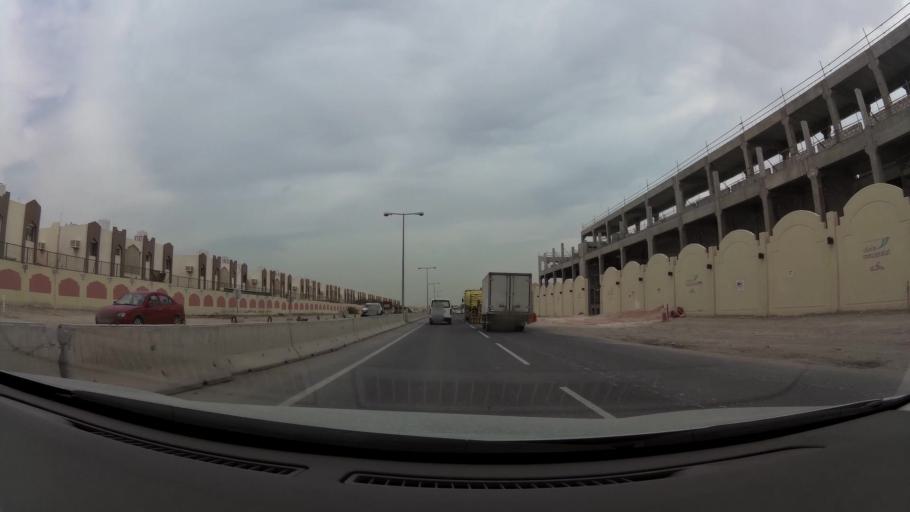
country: QA
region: Baladiyat ar Rayyan
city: Ar Rayyan
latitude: 25.2179
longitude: 51.4399
